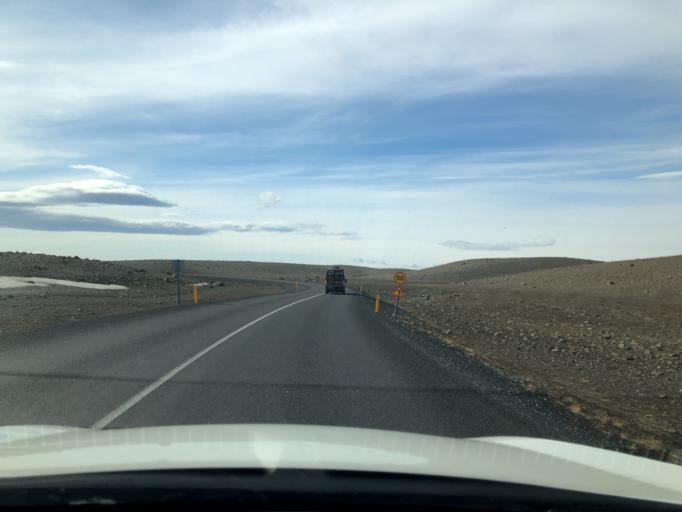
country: IS
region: Northeast
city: Husavik
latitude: 65.8145
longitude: -16.4087
